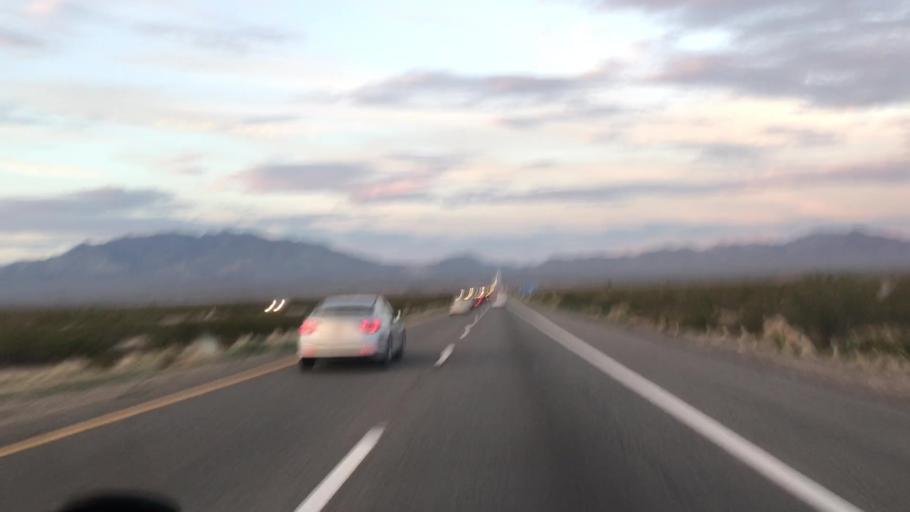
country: US
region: Nevada
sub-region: Clark County
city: Sandy Valley
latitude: 35.4213
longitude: -115.7382
